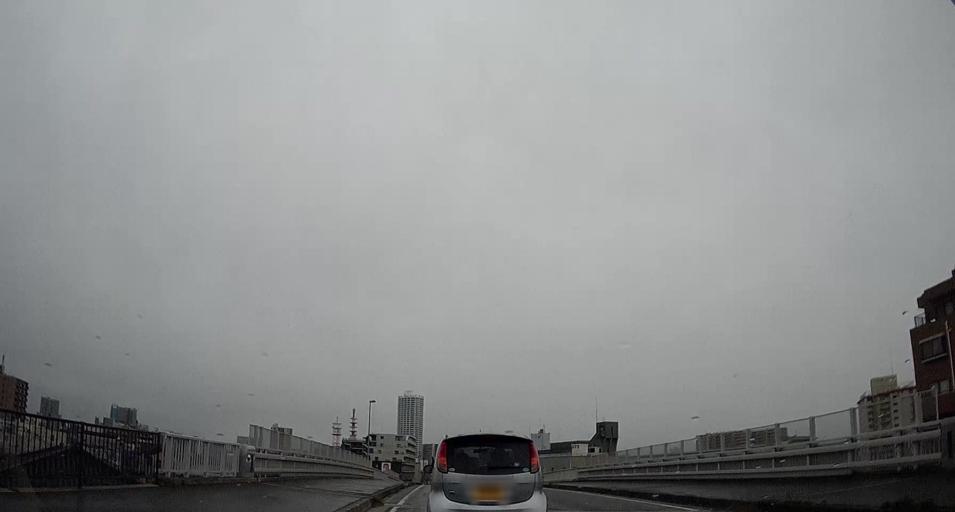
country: JP
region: Chiba
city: Funabashi
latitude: 35.7022
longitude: 139.9745
